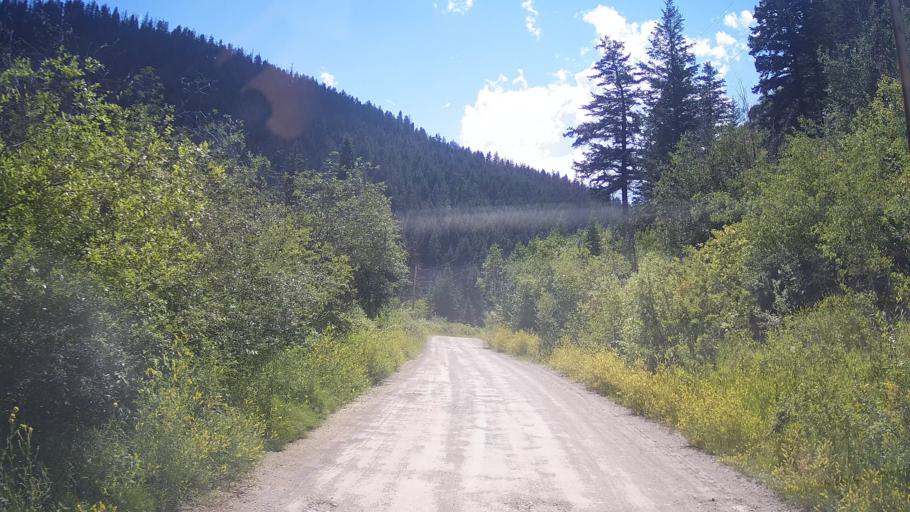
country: CA
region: British Columbia
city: Lillooet
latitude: 51.2568
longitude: -122.0002
